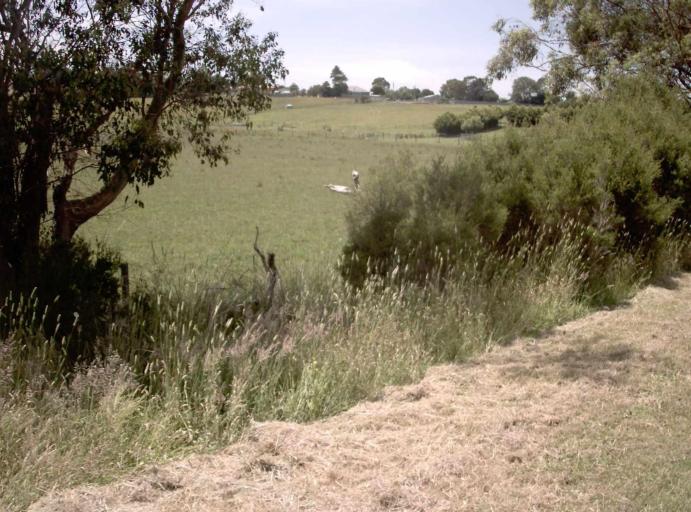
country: AU
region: Victoria
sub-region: Latrobe
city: Moe
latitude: -38.5306
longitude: 146.0893
